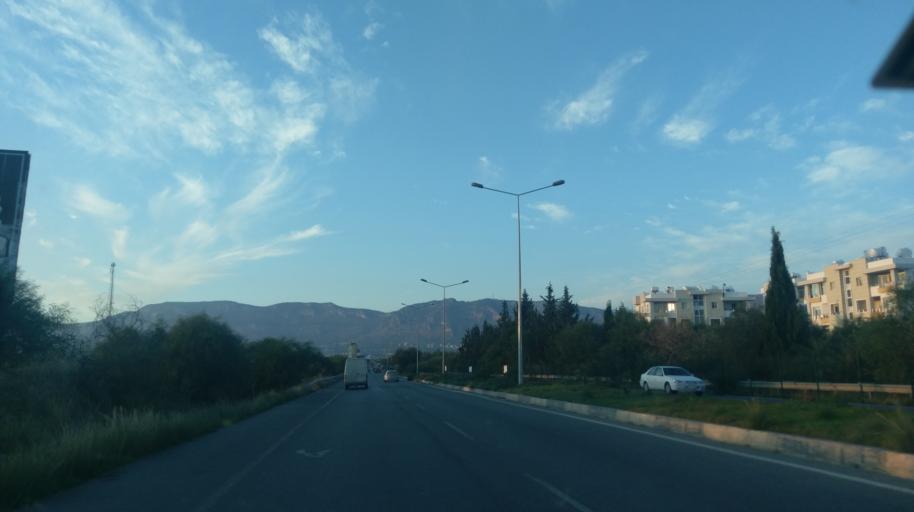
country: CY
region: Keryneia
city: Kyrenia
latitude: 35.2547
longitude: 33.3007
